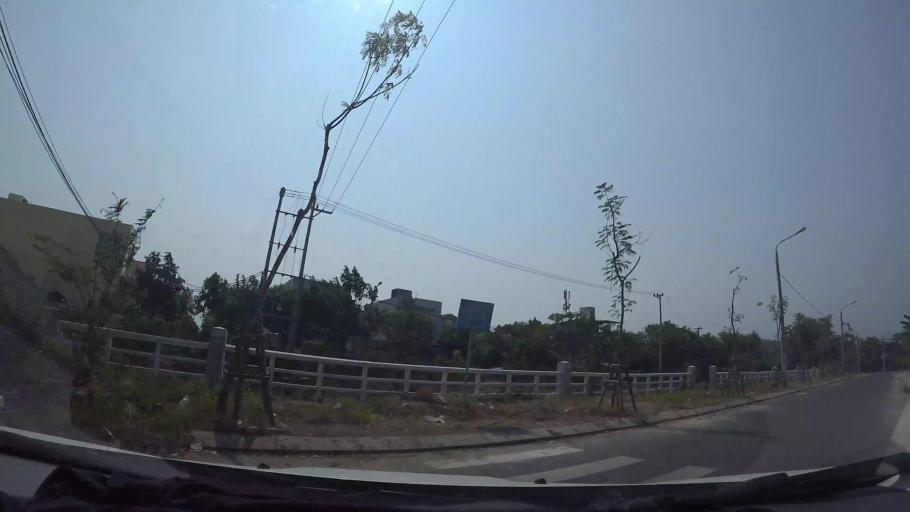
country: VN
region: Da Nang
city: Cam Le
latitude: 16.0090
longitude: 108.2005
